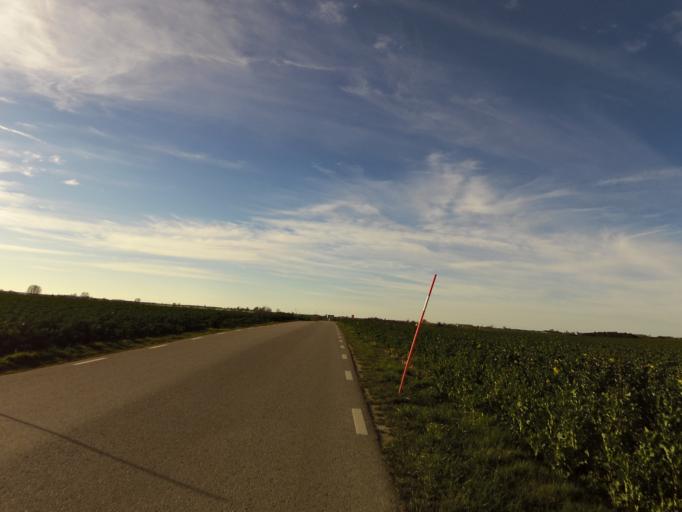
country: SE
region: Skane
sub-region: Kavlinge Kommun
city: Loddekopinge
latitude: 55.7575
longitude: 13.0630
